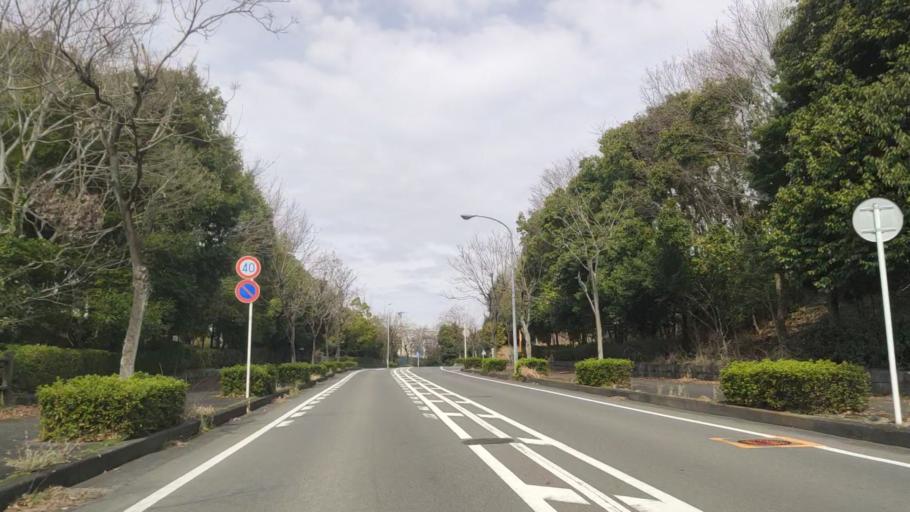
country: JP
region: Kanagawa
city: Hadano
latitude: 35.3452
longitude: 139.2219
